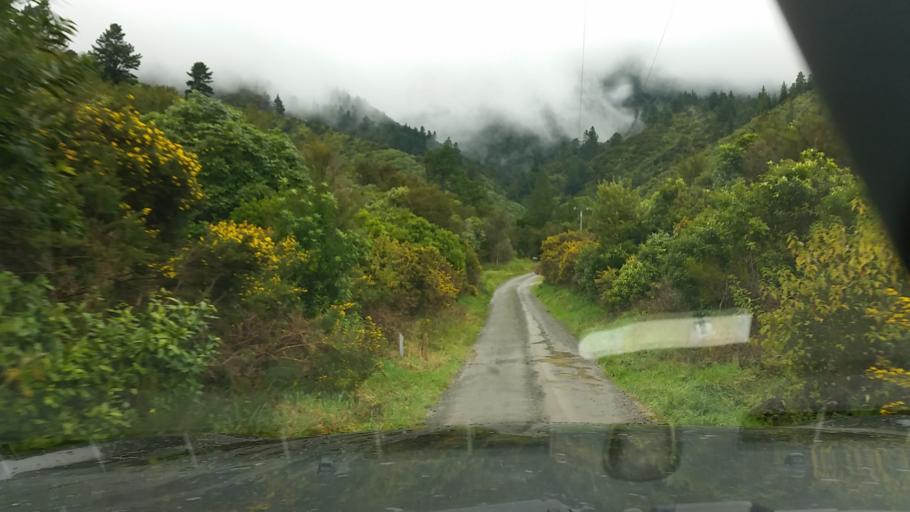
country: NZ
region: Marlborough
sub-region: Marlborough District
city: Picton
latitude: -41.2906
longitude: 174.0402
